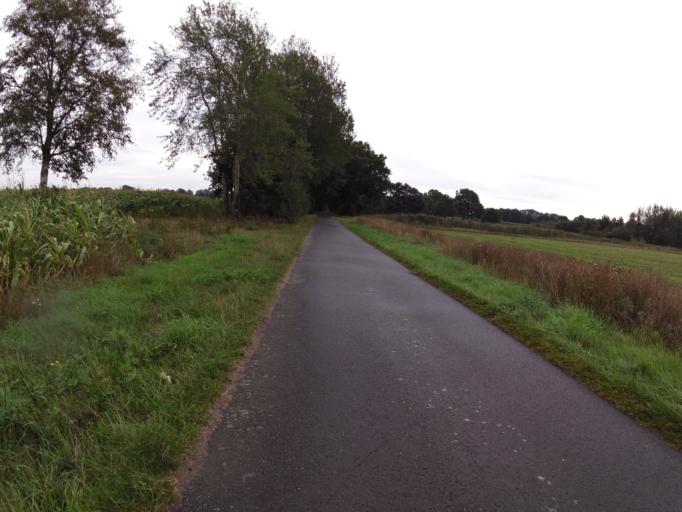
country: DE
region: Lower Saxony
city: Hamersen
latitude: 53.2657
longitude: 9.4740
